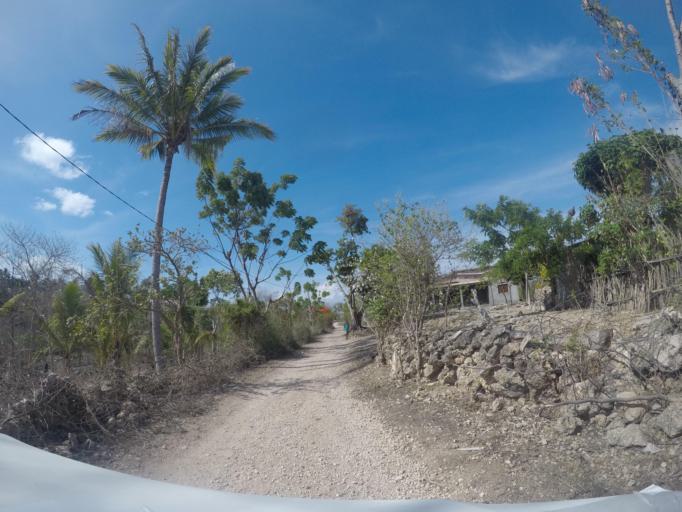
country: TL
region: Baucau
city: Baucau
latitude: -8.4630
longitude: 126.4697
